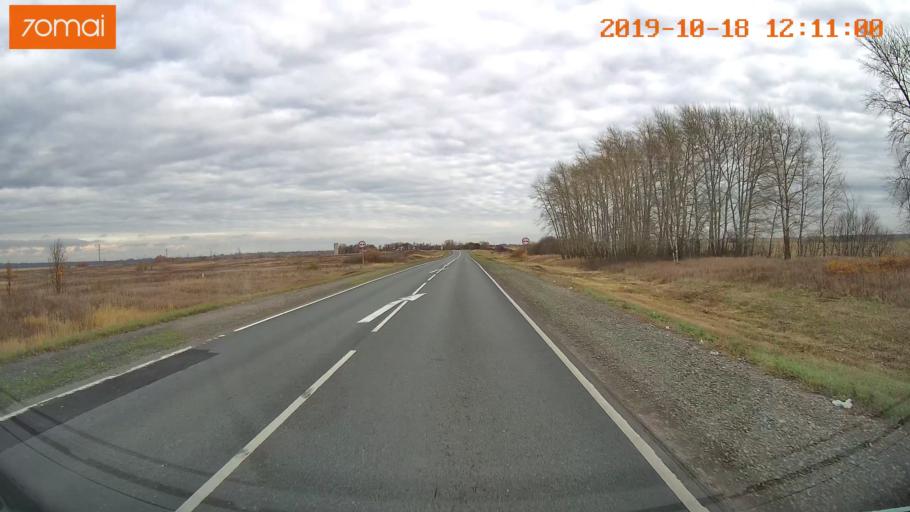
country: RU
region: Rjazan
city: Zakharovo
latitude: 54.3973
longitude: 39.3433
